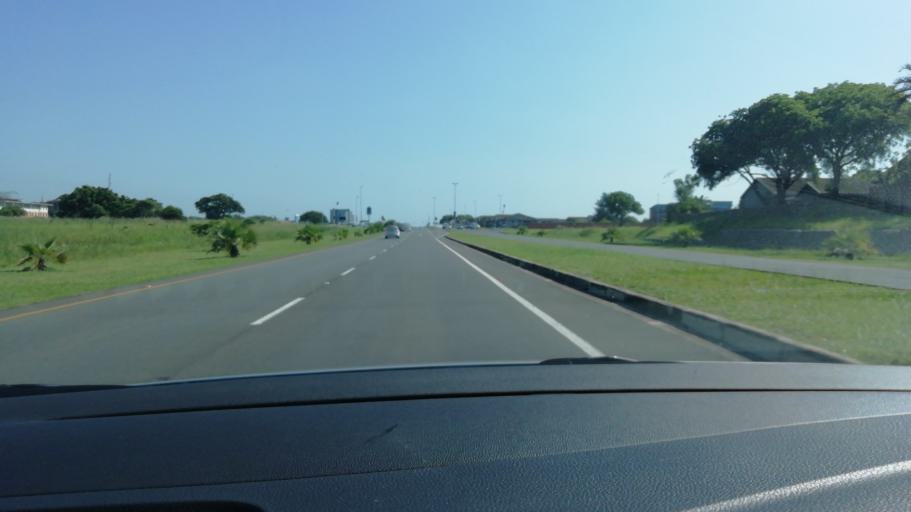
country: ZA
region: KwaZulu-Natal
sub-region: uThungulu District Municipality
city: Richards Bay
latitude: -28.7609
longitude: 32.0504
